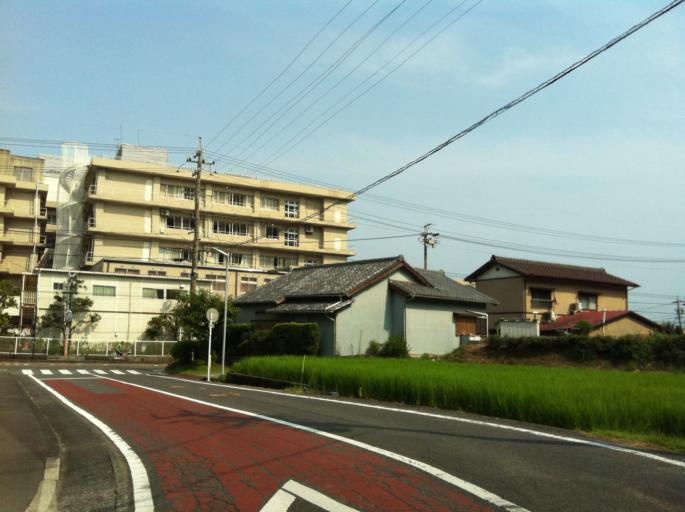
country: JP
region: Shizuoka
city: Shimada
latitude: 34.8465
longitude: 138.1818
